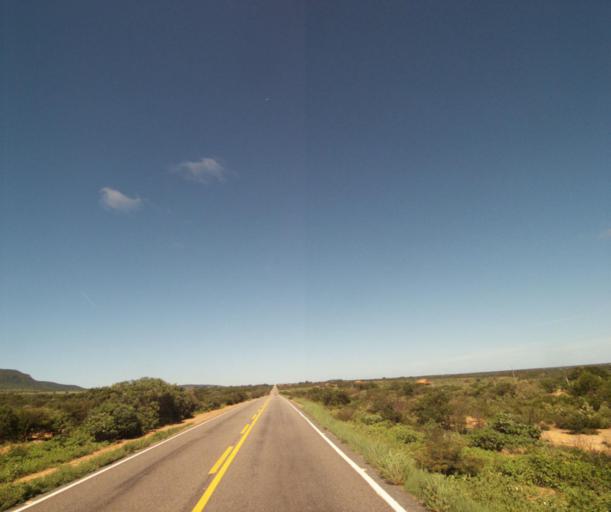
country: BR
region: Bahia
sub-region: Palmas De Monte Alto
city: Palmas de Monte Alto
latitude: -14.2457
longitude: -43.1160
